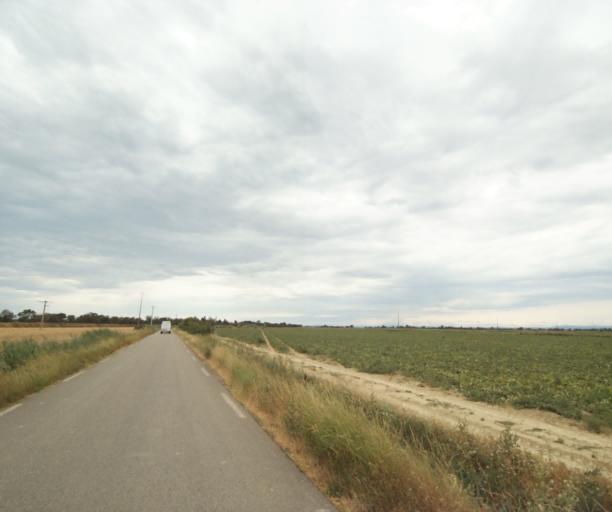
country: FR
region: Languedoc-Roussillon
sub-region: Departement de l'Herault
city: La Grande-Motte
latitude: 43.5984
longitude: 4.1204
